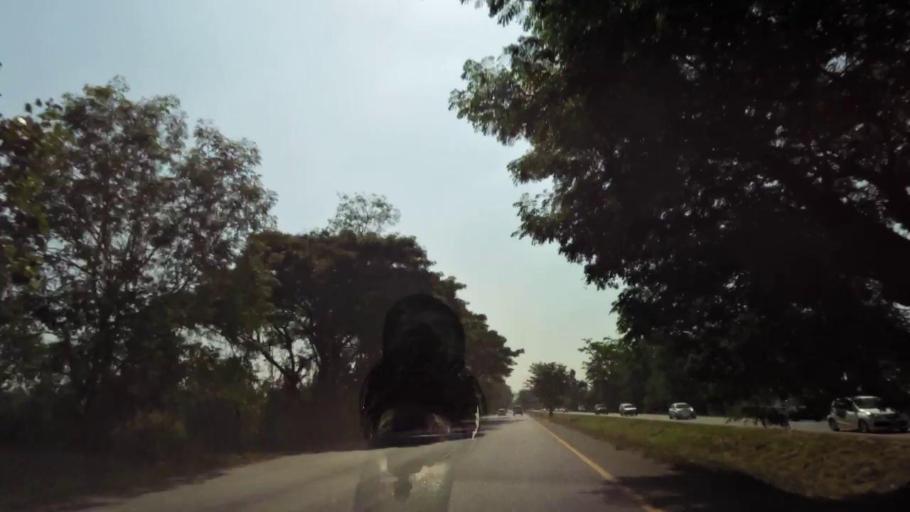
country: TH
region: Phichit
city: Wachira Barami
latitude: 16.3701
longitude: 100.1325
